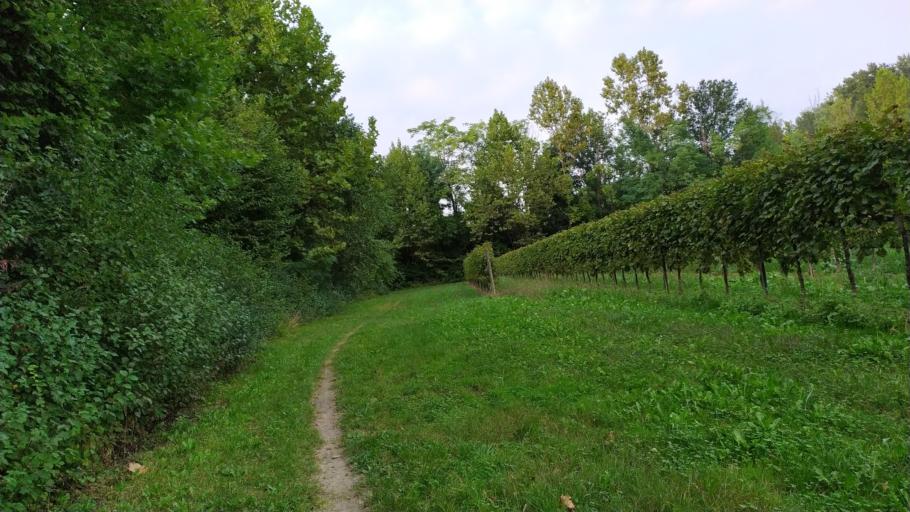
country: IT
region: Veneto
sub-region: Provincia di Treviso
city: Conegliano
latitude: 45.9054
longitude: 12.2945
